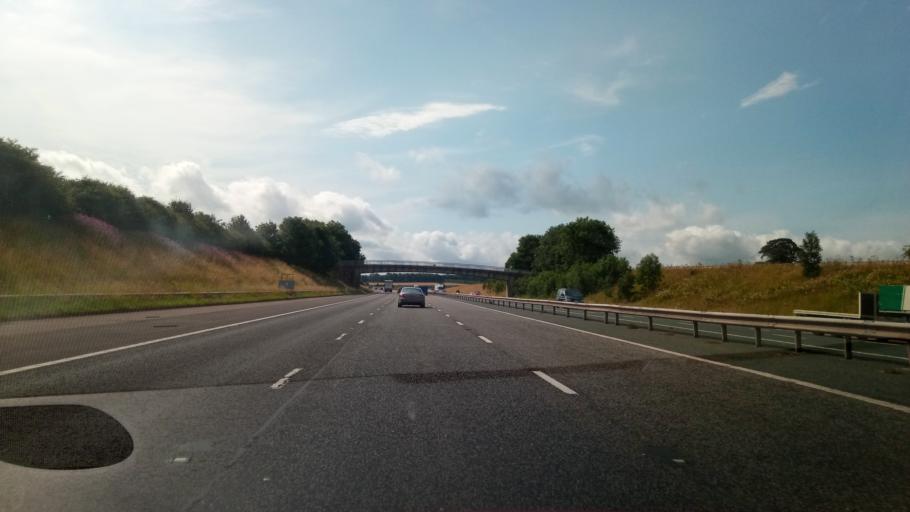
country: GB
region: England
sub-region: Cumbria
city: Penrith
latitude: 54.6246
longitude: -2.7222
